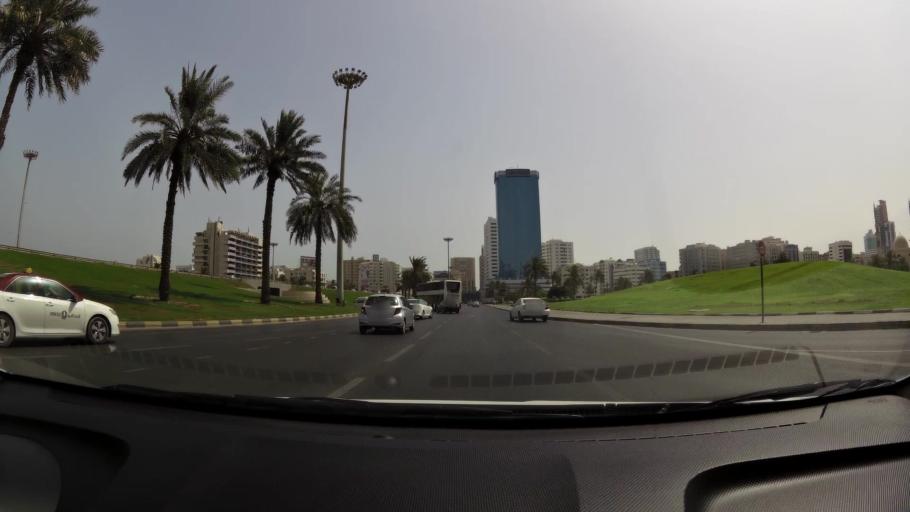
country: AE
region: Ash Shariqah
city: Sharjah
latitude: 25.3495
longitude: 55.3833
